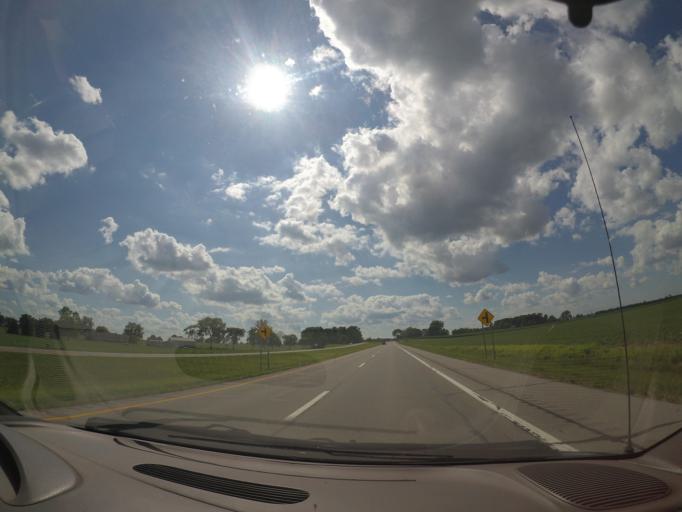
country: US
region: Ohio
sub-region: Huron County
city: Monroeville
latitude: 41.2553
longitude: -82.7390
